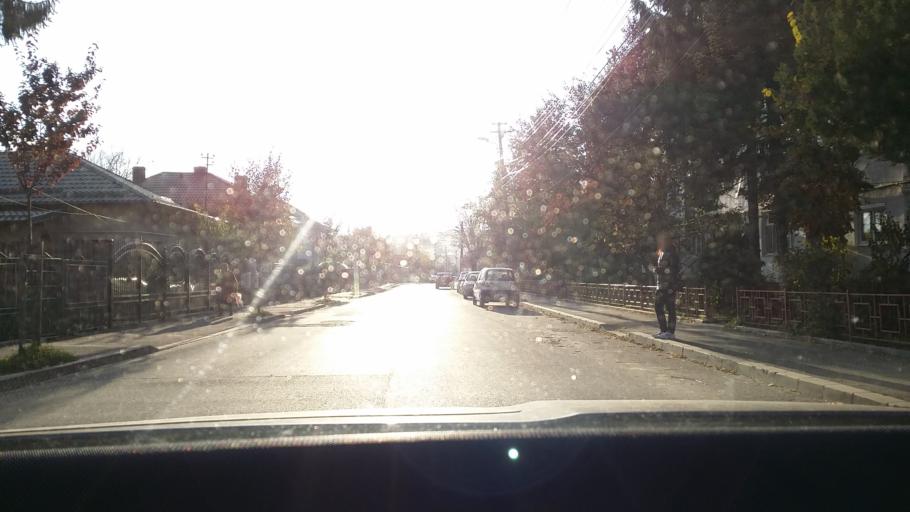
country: RO
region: Prahova
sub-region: Municipiul Campina
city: Campina
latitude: 45.1259
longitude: 25.7432
